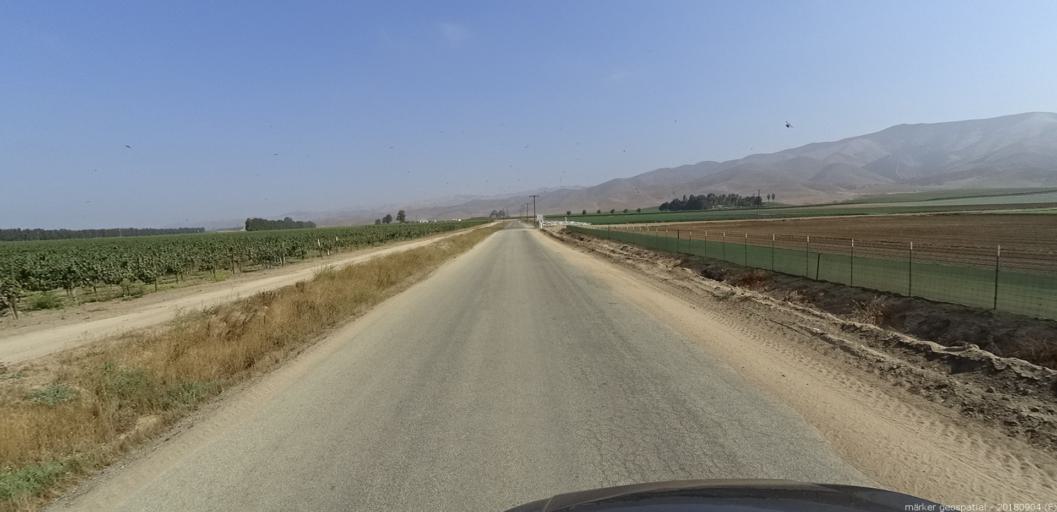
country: US
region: California
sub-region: Monterey County
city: Soledad
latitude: 36.4693
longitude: -121.3511
